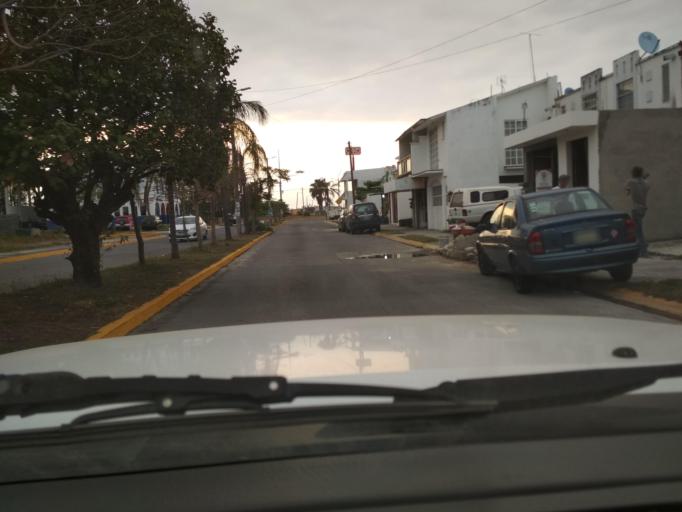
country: MX
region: Veracruz
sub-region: Medellin
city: Fraccionamiento Arboledas San Ramon
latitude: 19.0929
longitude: -96.1538
